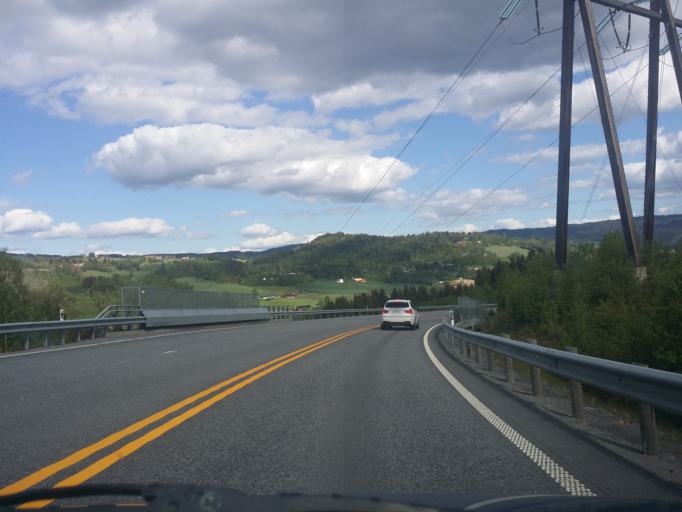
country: NO
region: Oppland
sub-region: Lunner
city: Roa
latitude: 60.2967
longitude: 10.5887
